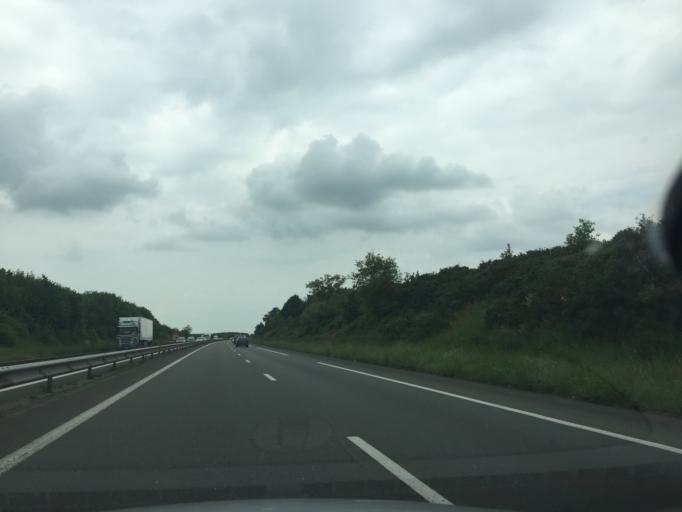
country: FR
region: Pays de la Loire
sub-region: Departement de la Loire-Atlantique
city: Aigrefeuille-sur-Maine
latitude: 47.0619
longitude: -1.4271
